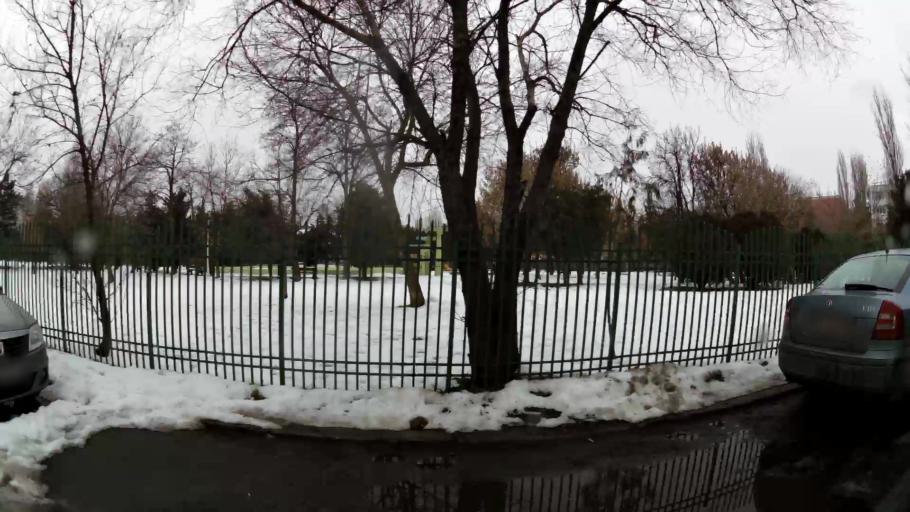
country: RO
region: Ilfov
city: Dobroesti
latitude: 44.4204
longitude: 26.1695
